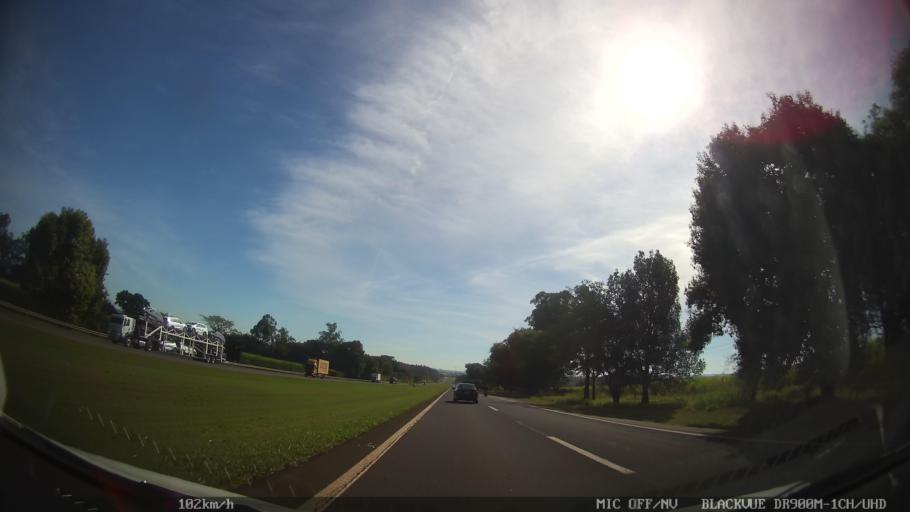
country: BR
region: Sao Paulo
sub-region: Leme
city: Leme
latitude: -22.2402
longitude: -47.3906
